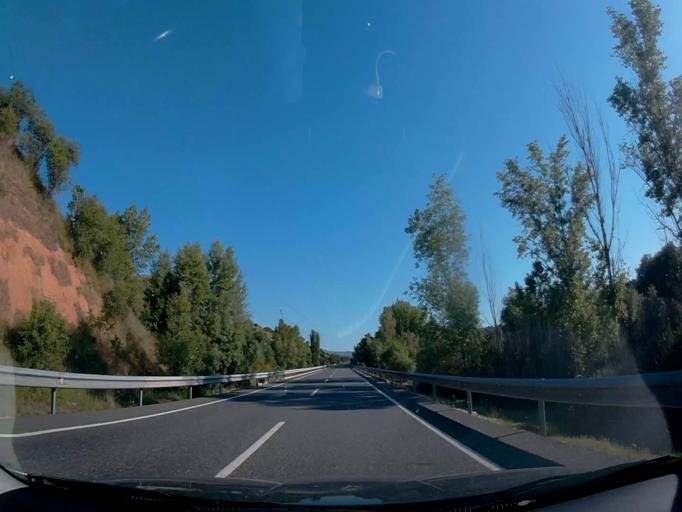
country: ES
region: Castille-La Mancha
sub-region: Province of Toledo
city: Escalona
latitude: 40.1729
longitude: -4.3994
